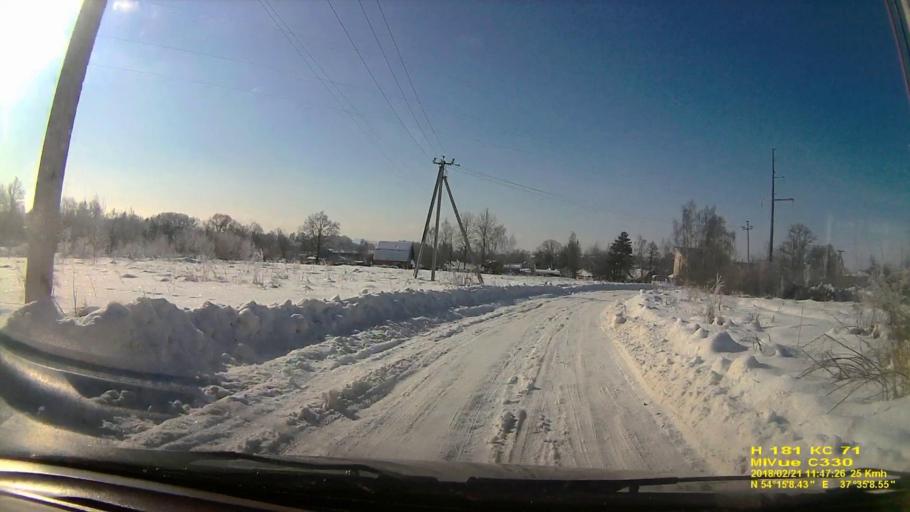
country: RU
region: Tula
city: Gorelki
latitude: 54.2524
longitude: 37.5854
